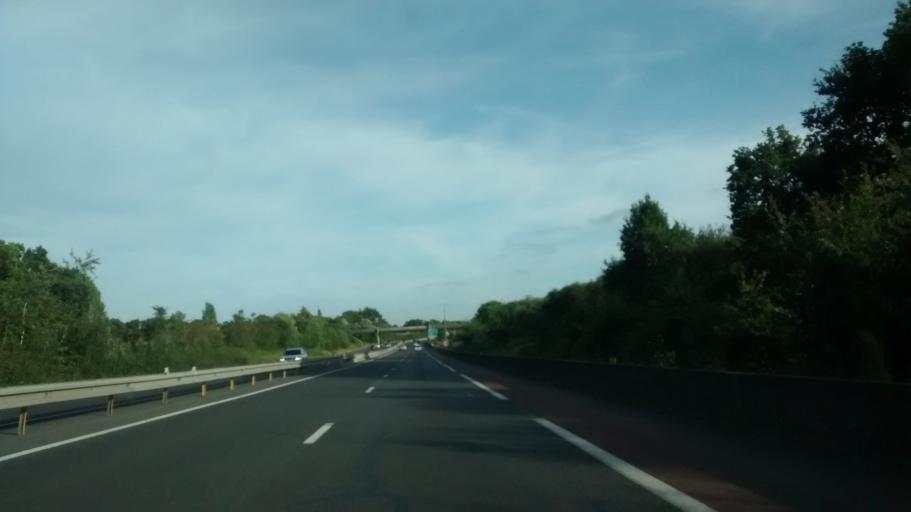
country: FR
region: Lower Normandy
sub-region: Departement de la Manche
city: Le Val-Saint-Pere
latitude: 48.6675
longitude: -1.3705
